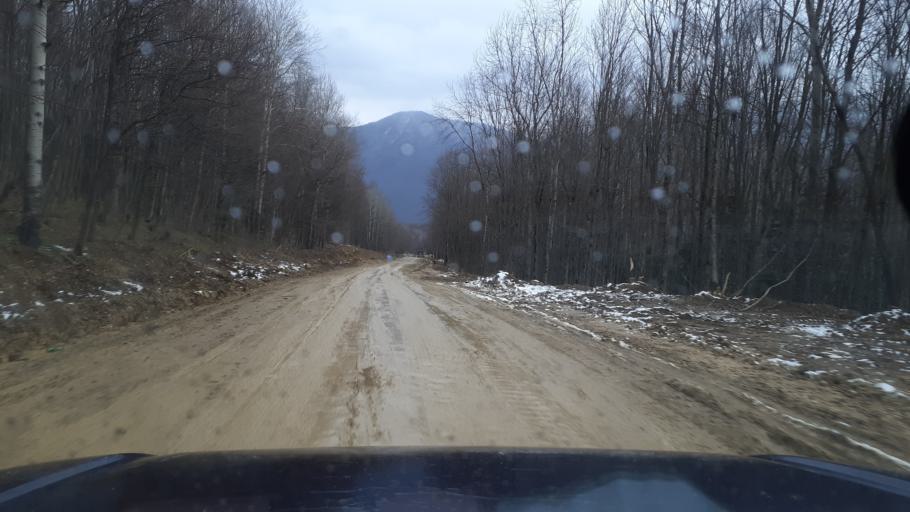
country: RU
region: Krasnodarskiy
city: Neftegorsk
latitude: 44.1621
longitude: 39.7968
